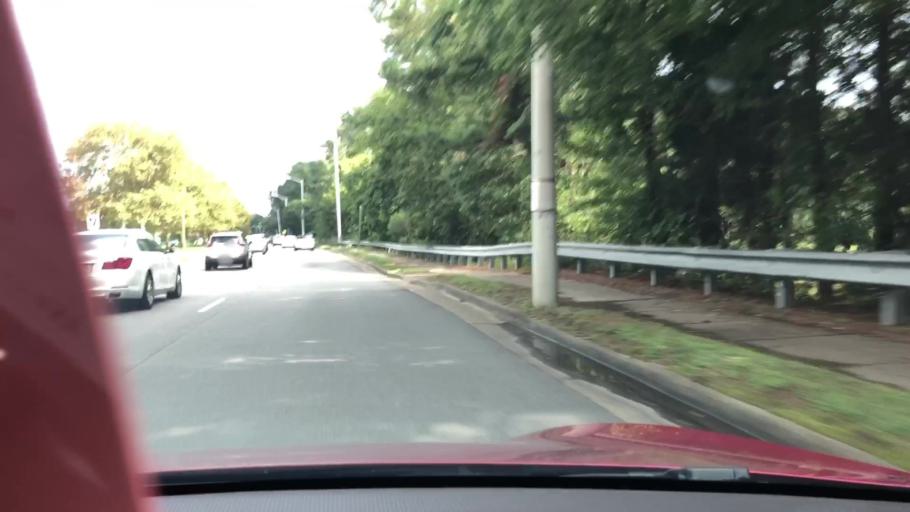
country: US
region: Virginia
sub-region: City of Virginia Beach
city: Virginia Beach
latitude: 36.8978
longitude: -76.0639
